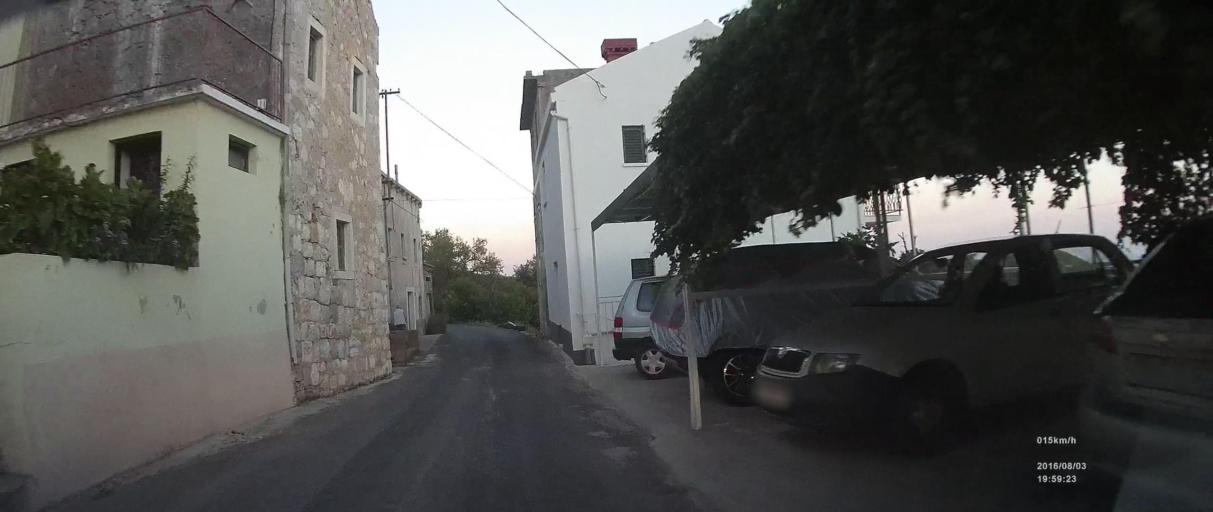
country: HR
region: Dubrovacko-Neretvanska
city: Blato
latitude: 42.7329
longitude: 17.5583
